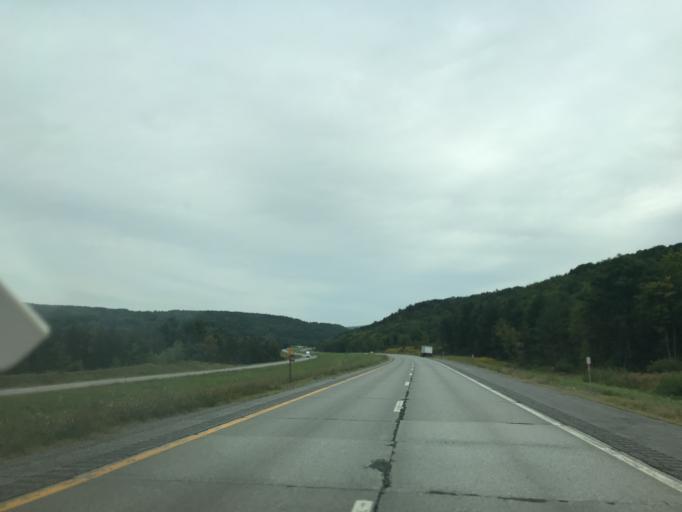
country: US
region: New York
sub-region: Schoharie County
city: Cobleskill
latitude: 42.6489
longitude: -74.6205
